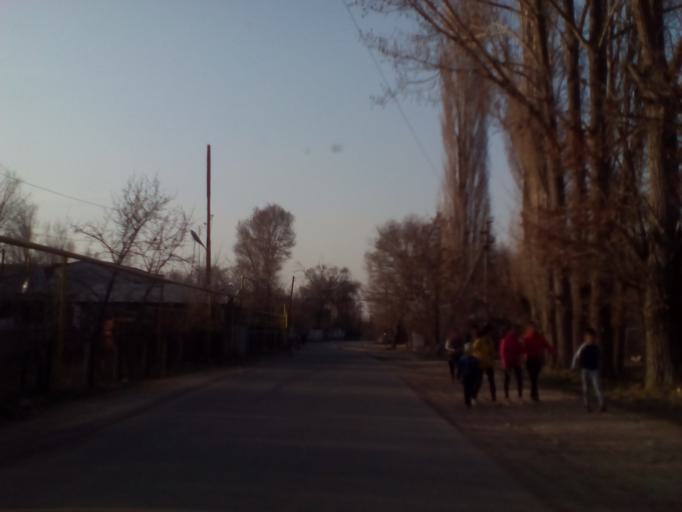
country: KZ
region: Almaty Oblysy
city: Burunday
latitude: 43.1570
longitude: 76.4213
